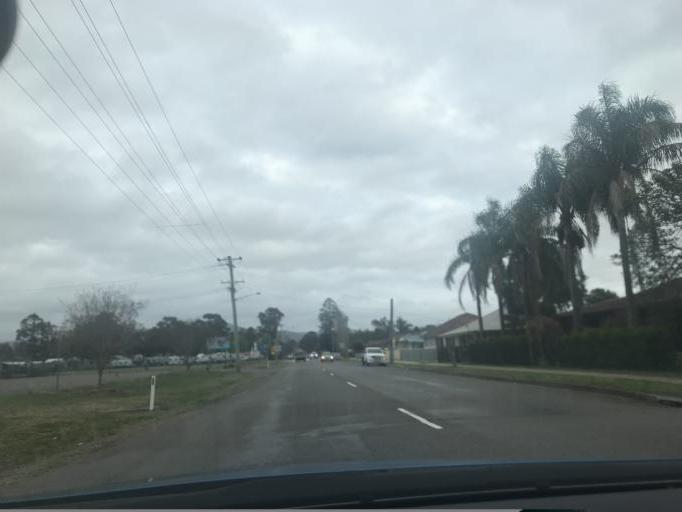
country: AU
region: New South Wales
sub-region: Cessnock
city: Cessnock
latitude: -32.8309
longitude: 151.3415
